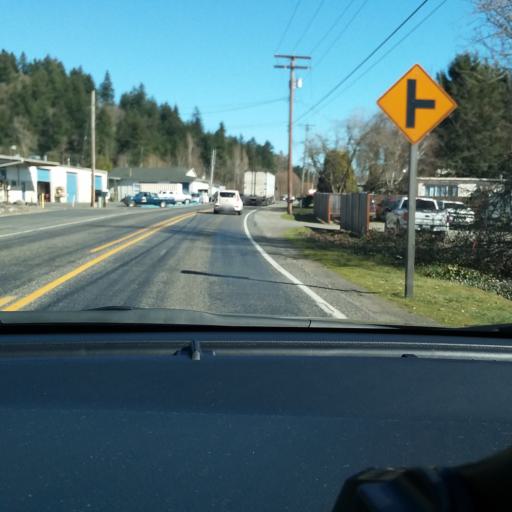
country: US
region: Washington
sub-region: Pierce County
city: North Puyallup
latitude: 47.2073
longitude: -122.2785
